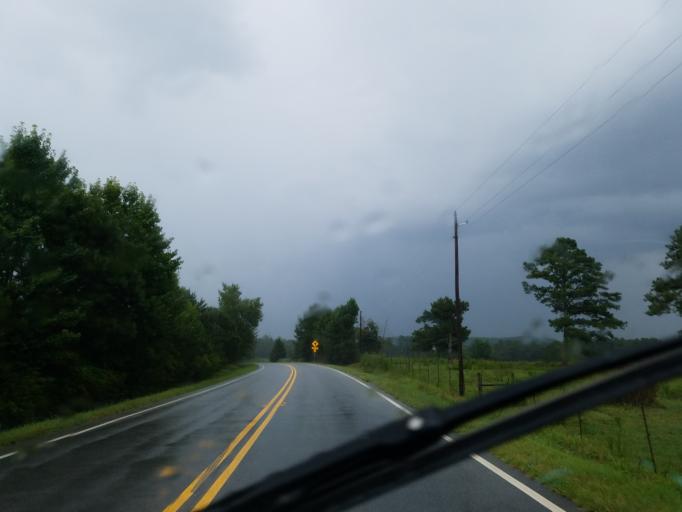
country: US
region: Georgia
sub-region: Floyd County
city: Shannon
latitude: 34.3726
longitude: -85.0999
